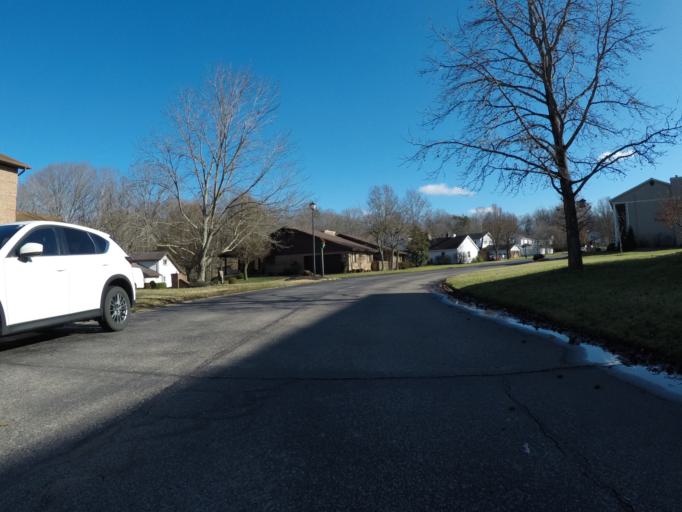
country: US
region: West Virginia
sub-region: Cabell County
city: Pea Ridge
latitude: 38.4187
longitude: -82.3266
